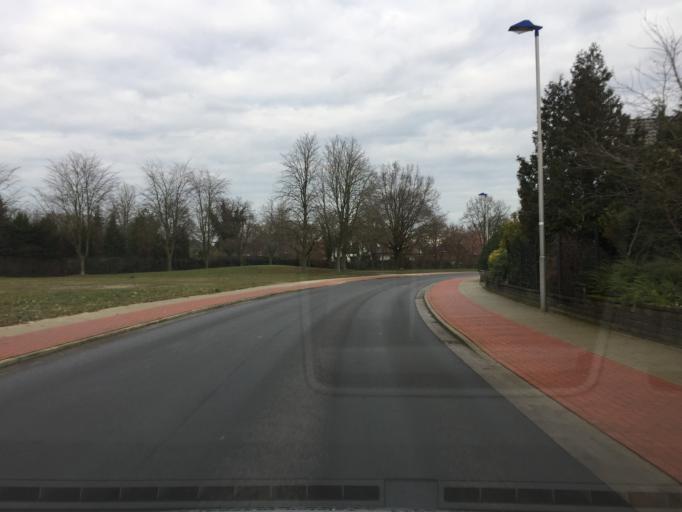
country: DE
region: Lower Saxony
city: Sulingen
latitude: 52.6788
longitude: 8.8190
